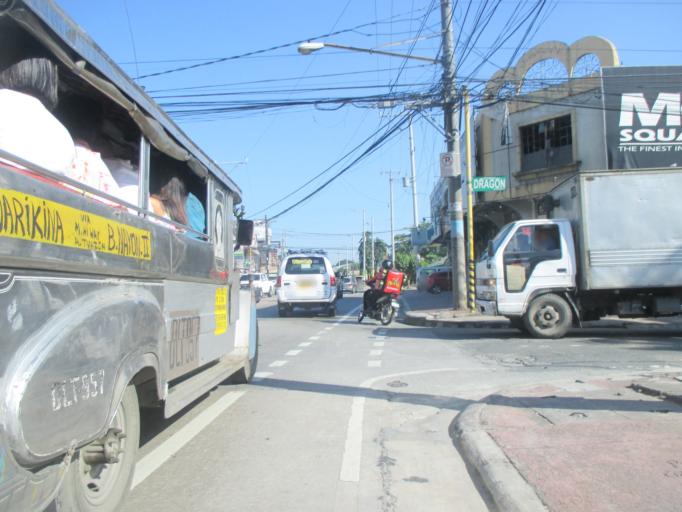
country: PH
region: Metro Manila
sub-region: Marikina
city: Calumpang
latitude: 14.6237
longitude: 121.1023
